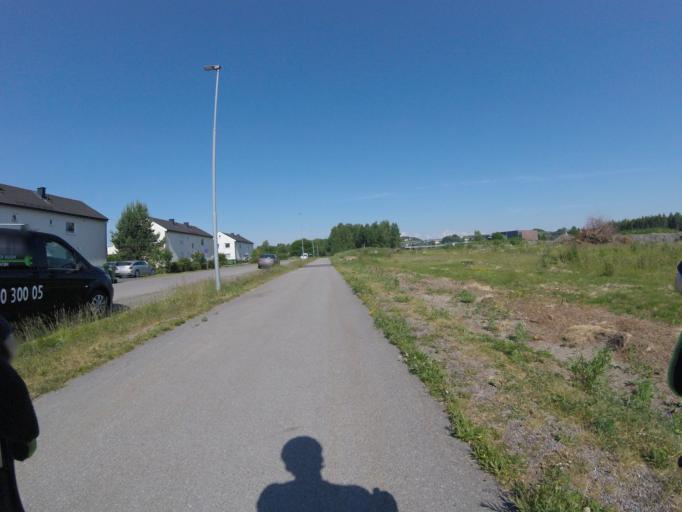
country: NO
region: Akershus
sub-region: Skedsmo
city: Lillestrom
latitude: 59.9656
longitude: 11.0374
